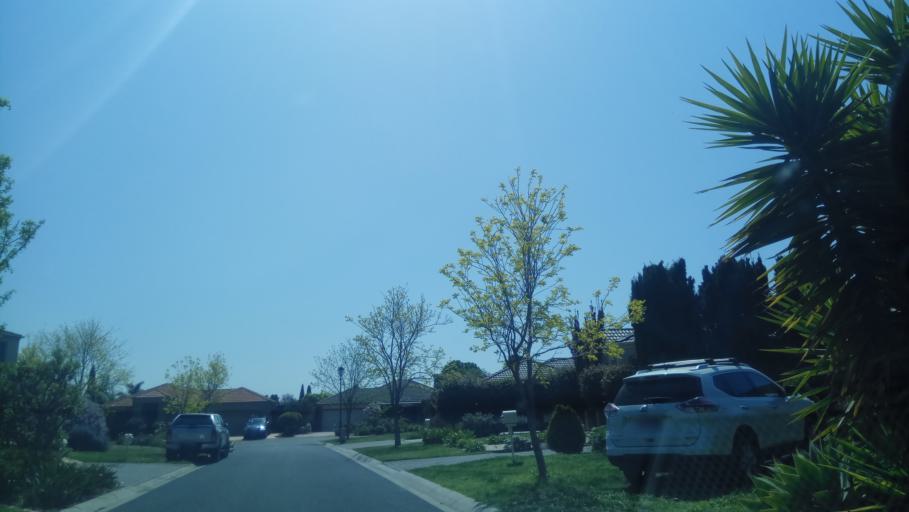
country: AU
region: Victoria
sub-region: Wyndham
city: Point Cook
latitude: -37.8962
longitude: 144.7504
